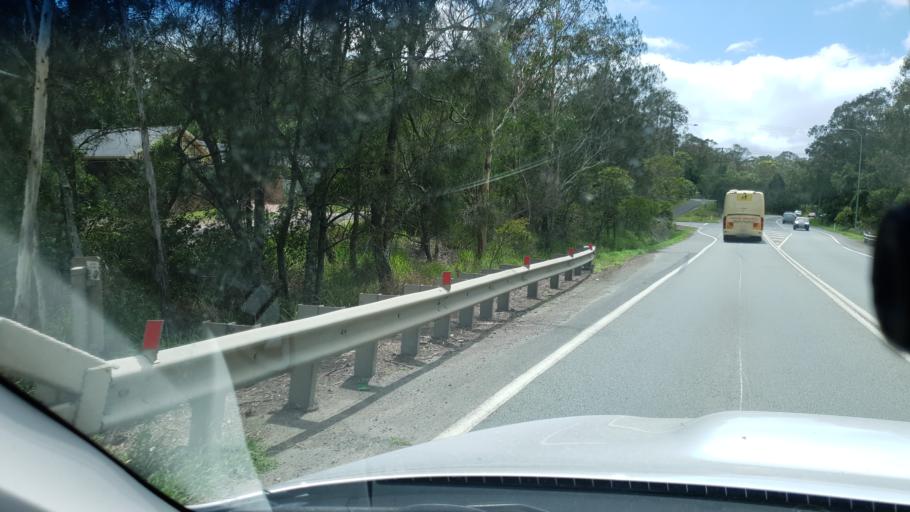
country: AU
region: Queensland
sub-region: Logan
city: Beenleigh
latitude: -27.6732
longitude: 153.2164
